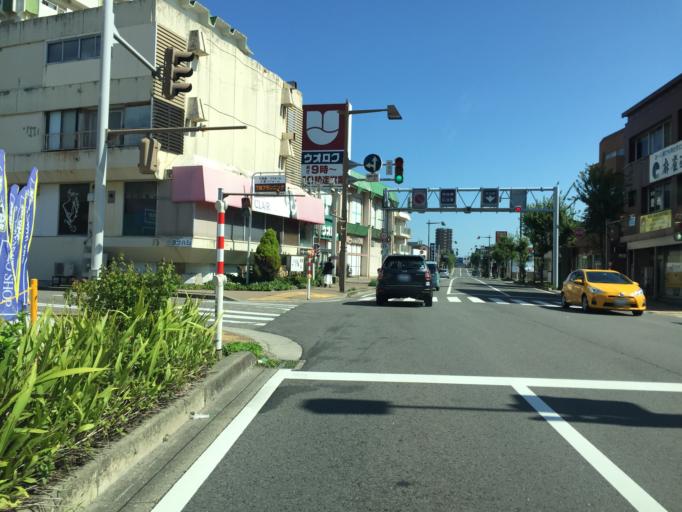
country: JP
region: Niigata
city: Niigata-shi
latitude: 37.9056
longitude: 139.0125
